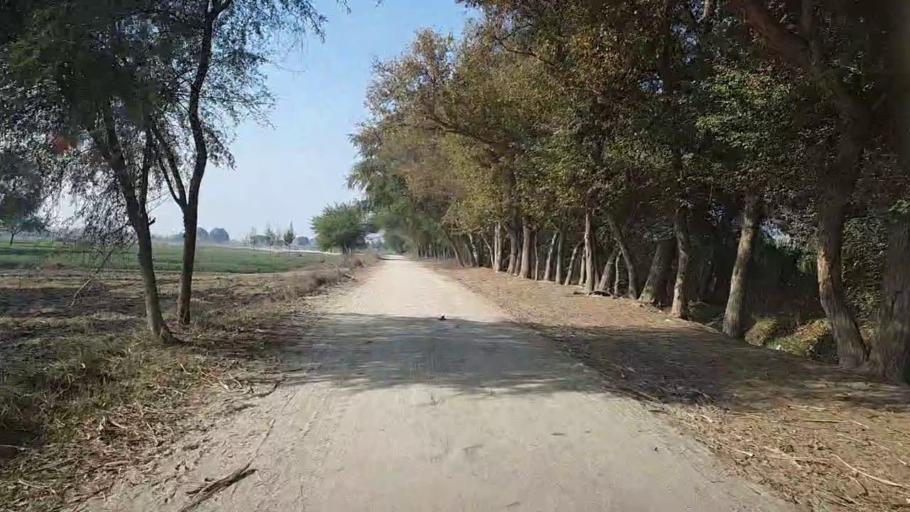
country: PK
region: Sindh
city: Mirpur Mathelo
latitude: 27.8979
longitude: 69.6504
